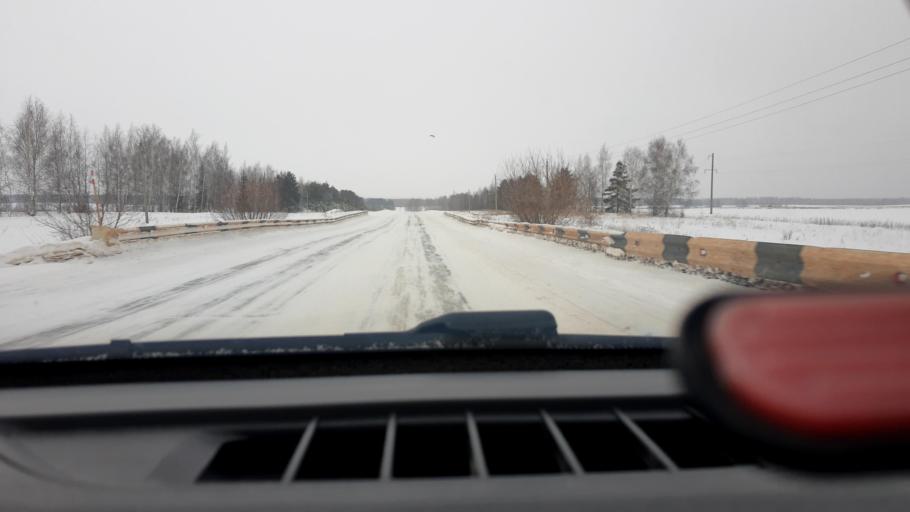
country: RU
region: Nizjnij Novgorod
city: Buturlino
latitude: 55.6076
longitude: 44.8613
